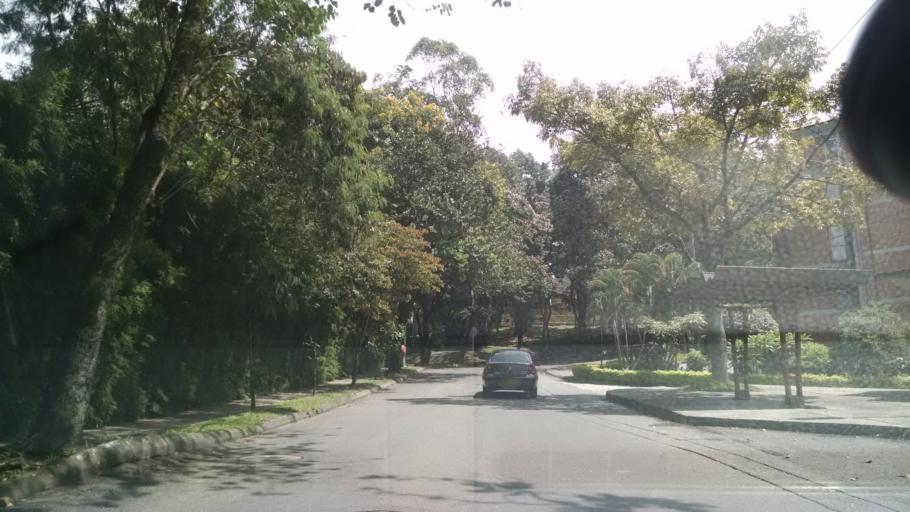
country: CO
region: Antioquia
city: Medellin
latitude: 6.2324
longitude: -75.5677
